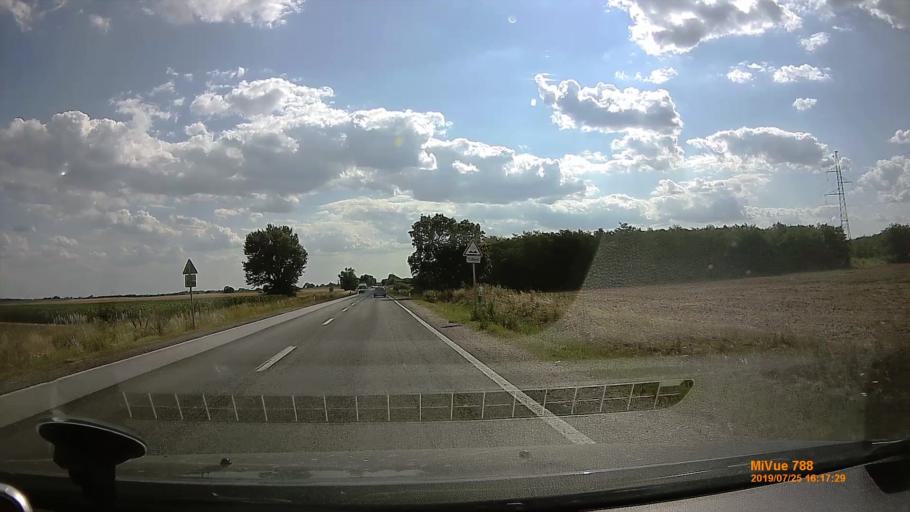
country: HU
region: Heves
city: Kal
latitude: 47.7689
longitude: 20.2746
